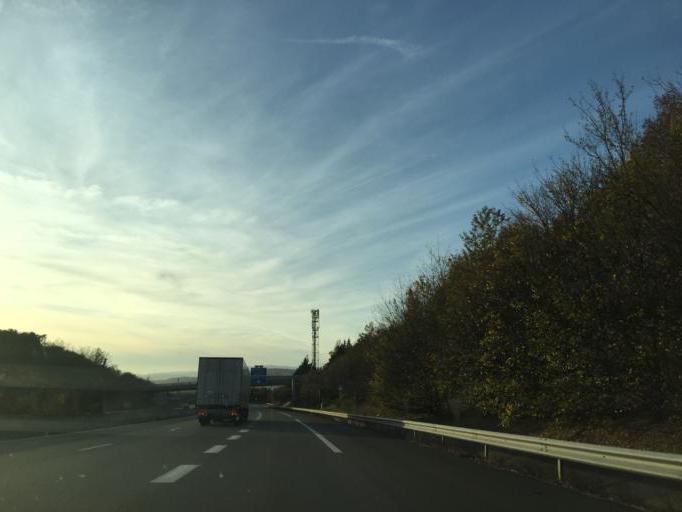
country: FR
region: Rhone-Alpes
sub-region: Departement de l'Isere
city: Chasse-sur-Rhone
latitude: 45.5895
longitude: 4.8067
